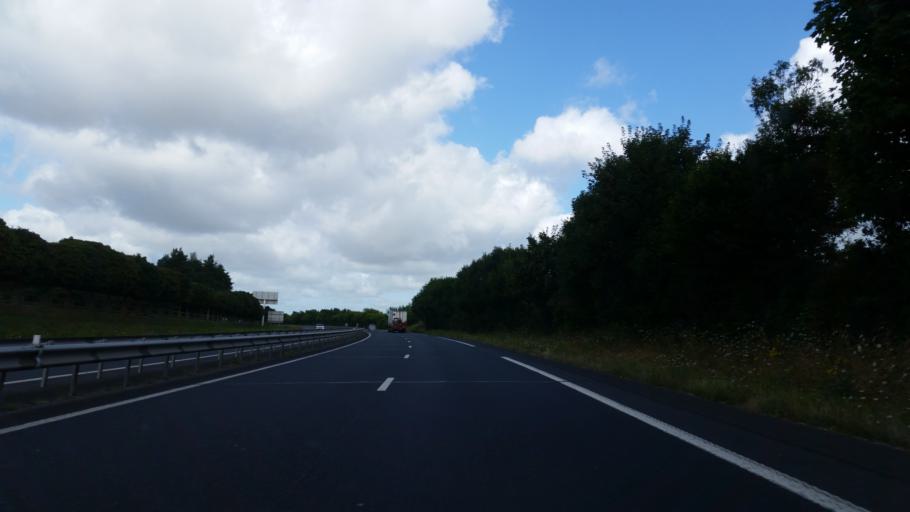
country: FR
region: Lower Normandy
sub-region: Departement du Calvados
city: Grandcamp-Maisy
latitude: 49.3422
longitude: -1.0186
